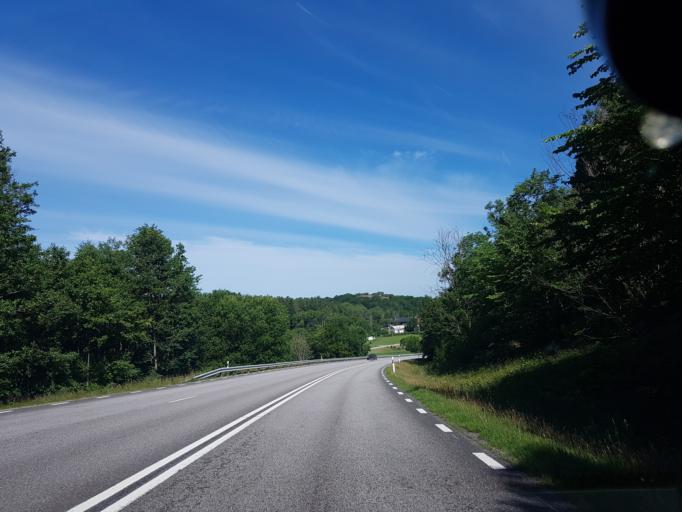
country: SE
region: Vaestra Goetaland
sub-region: Lysekils Kommun
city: Lysekil
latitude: 58.1644
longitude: 11.4864
